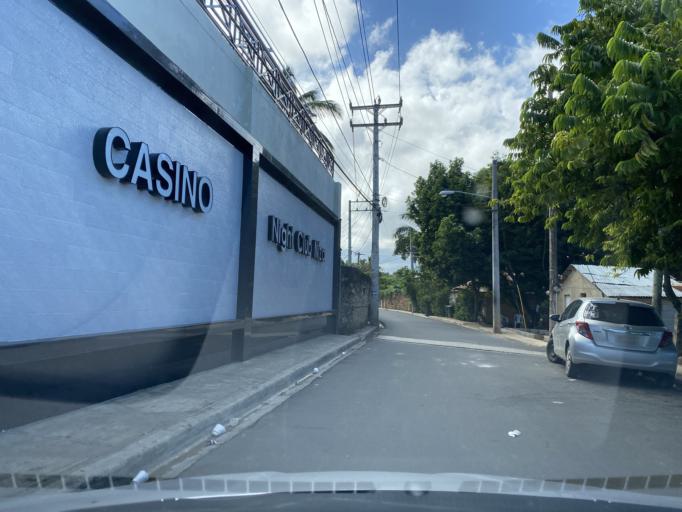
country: DO
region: Samana
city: Las Terrenas
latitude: 19.3093
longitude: -69.5511
